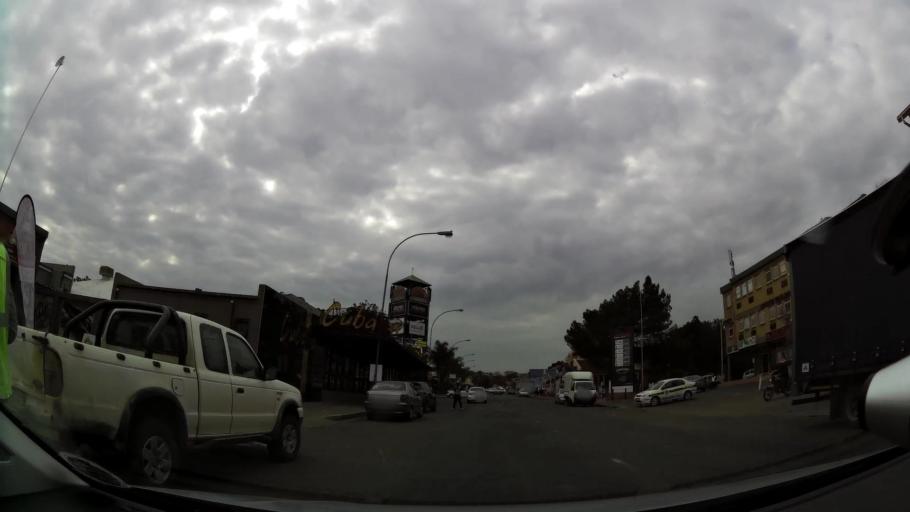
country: ZA
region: Orange Free State
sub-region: Mangaung Metropolitan Municipality
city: Bloemfontein
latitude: -29.1085
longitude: 26.2093
